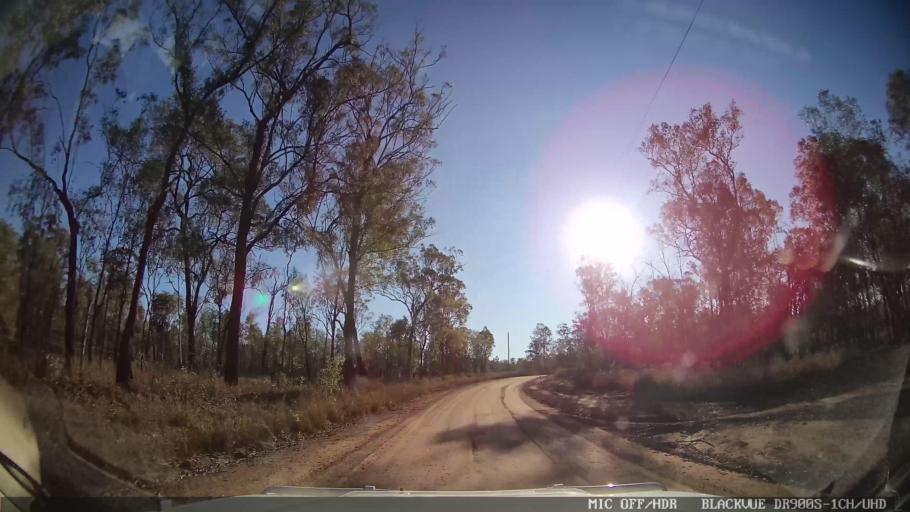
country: AU
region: Queensland
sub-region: Bundaberg
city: Sharon
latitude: -24.7404
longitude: 151.5266
